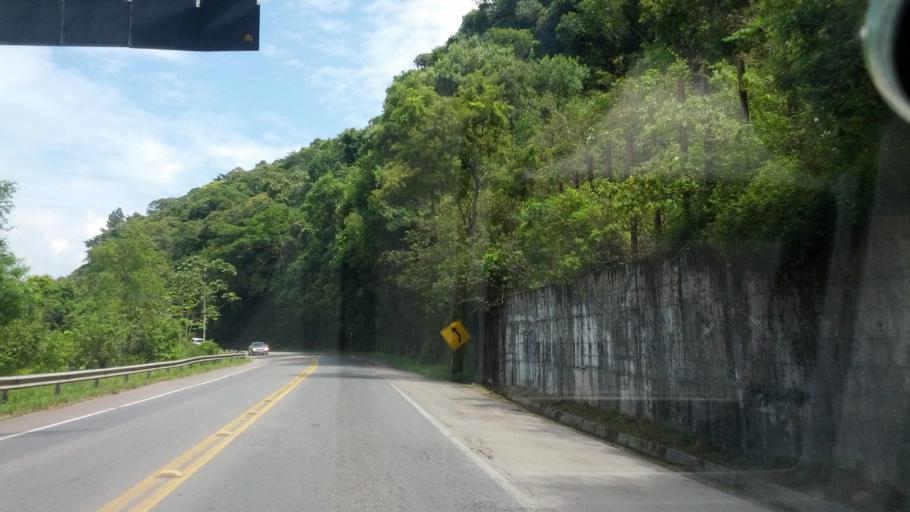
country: BR
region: Santa Catarina
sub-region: Ibirama
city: Ibirama
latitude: -27.0818
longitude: -49.5018
